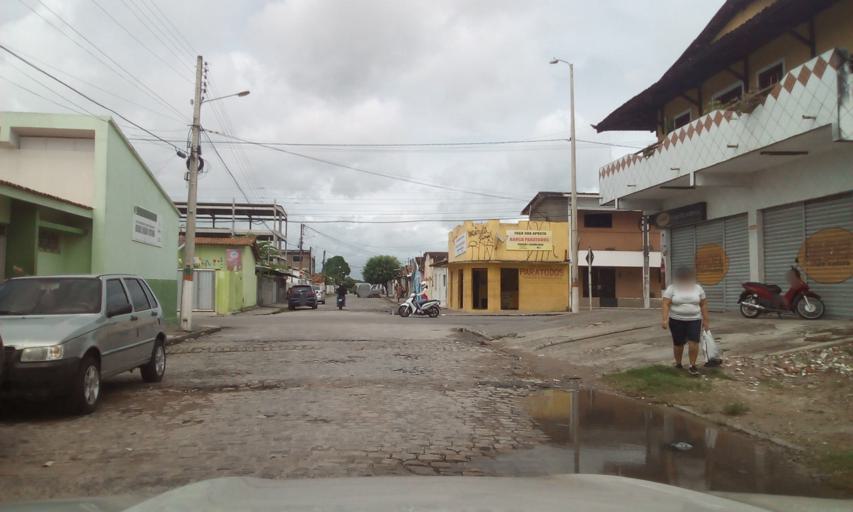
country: BR
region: Paraiba
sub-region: Bayeux
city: Bayeux
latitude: -7.1221
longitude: -34.9067
